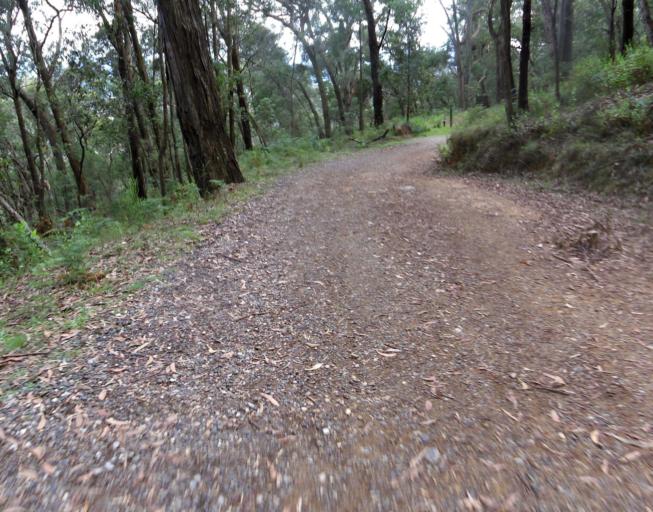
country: AU
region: Victoria
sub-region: Yarra Ranges
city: Montrose
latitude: -37.8372
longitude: 145.3426
